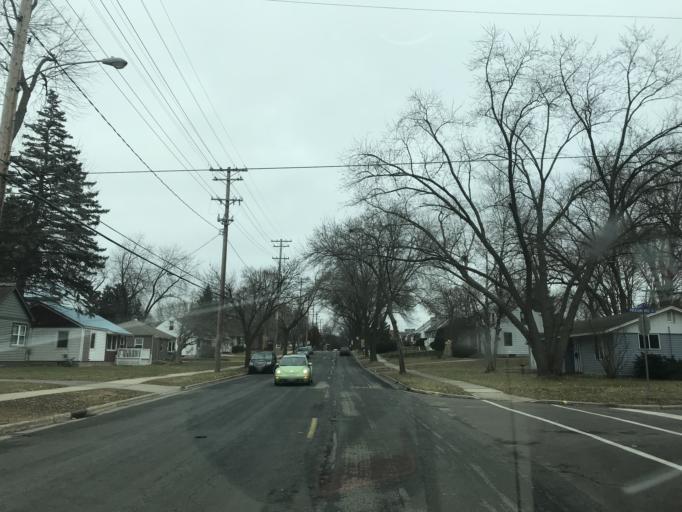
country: US
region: Wisconsin
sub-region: Dane County
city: Monona
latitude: 43.0623
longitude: -89.3313
